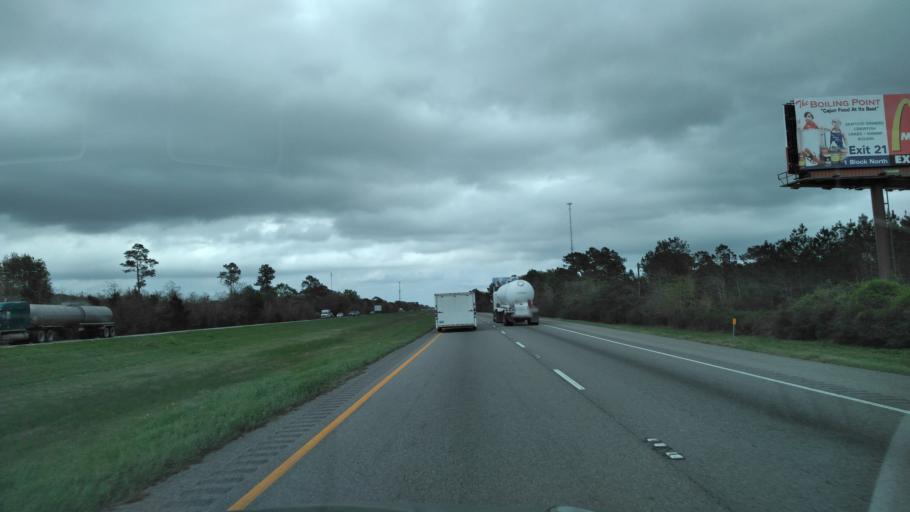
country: US
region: Louisiana
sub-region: Calcasieu Parish
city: Vinton
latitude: 30.1626
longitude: -93.6193
